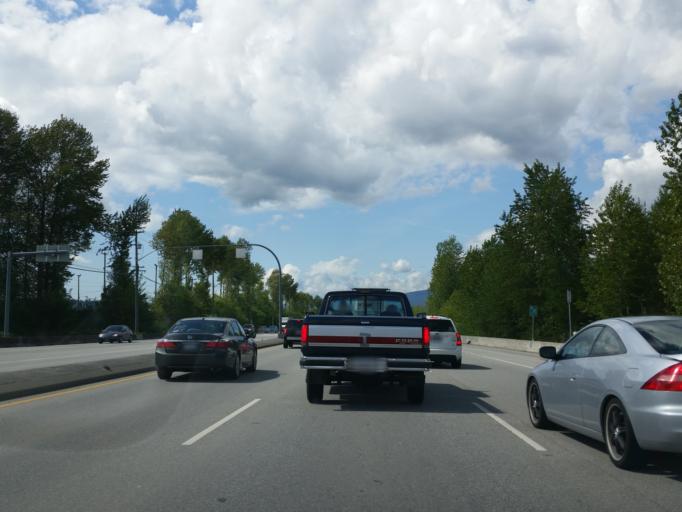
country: CA
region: British Columbia
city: Coquitlam
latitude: 49.2535
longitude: -122.7426
